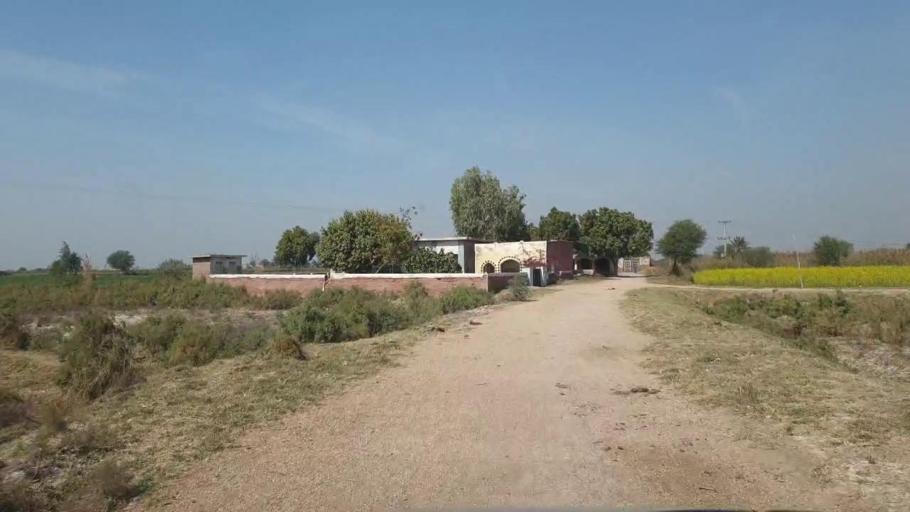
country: PK
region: Sindh
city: Chambar
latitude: 25.3402
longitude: 68.8367
